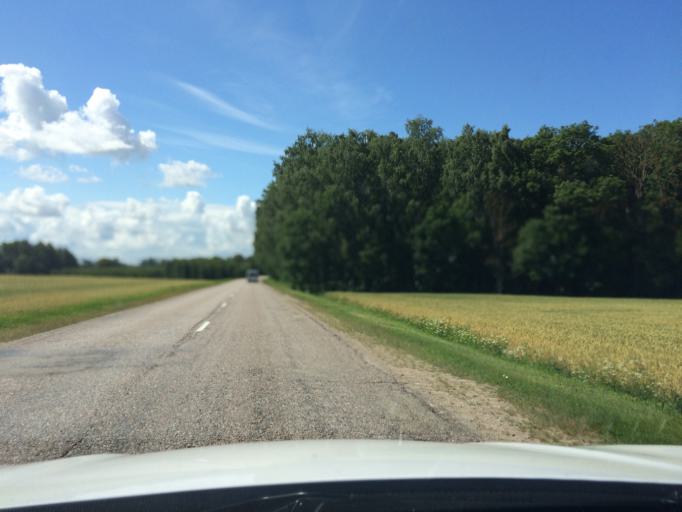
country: LV
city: Tervete
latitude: 56.5196
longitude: 23.4922
